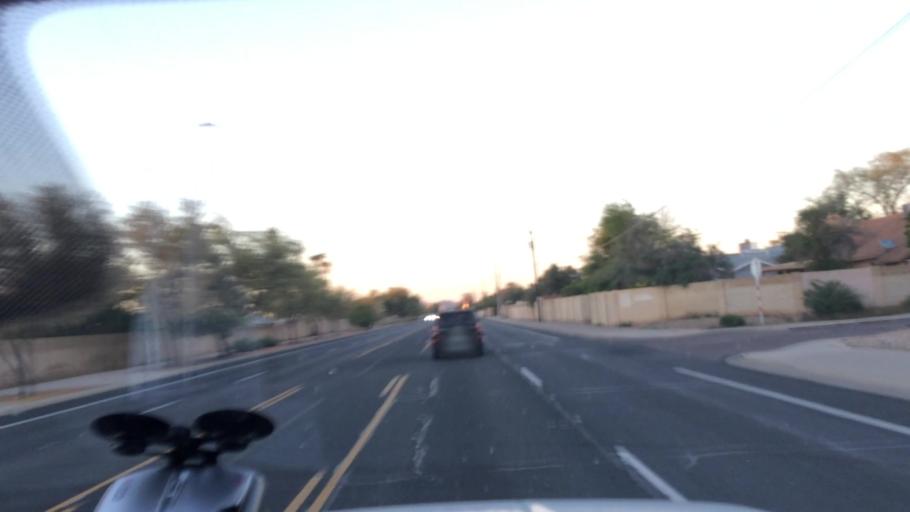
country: US
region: Arizona
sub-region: Maricopa County
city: Glendale
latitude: 33.6566
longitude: -112.0828
